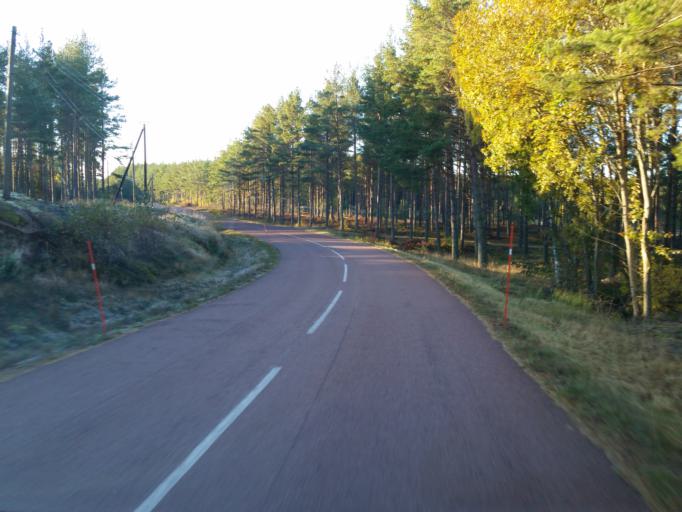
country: AX
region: Alands skaergard
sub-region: Vardoe
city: Vardoe
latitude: 60.2836
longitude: 20.3884
